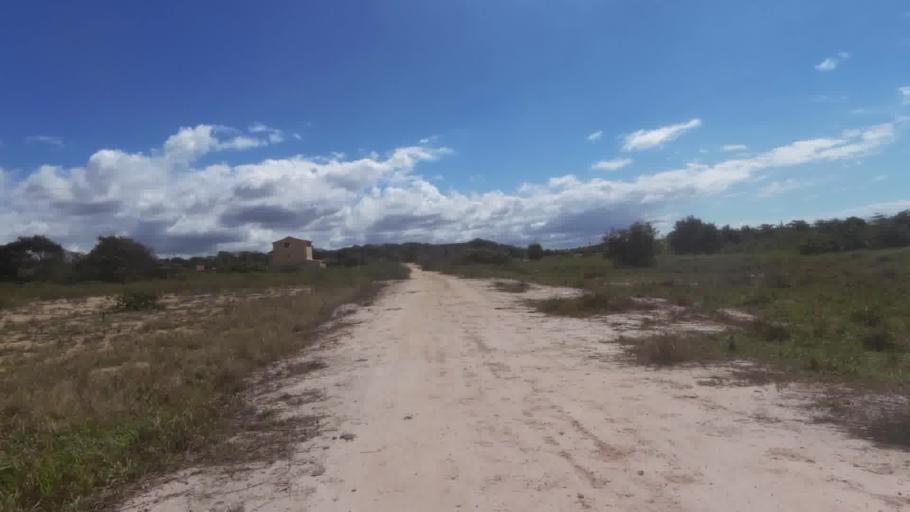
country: BR
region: Espirito Santo
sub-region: Marataizes
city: Marataizes
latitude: -21.2780
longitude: -40.9688
